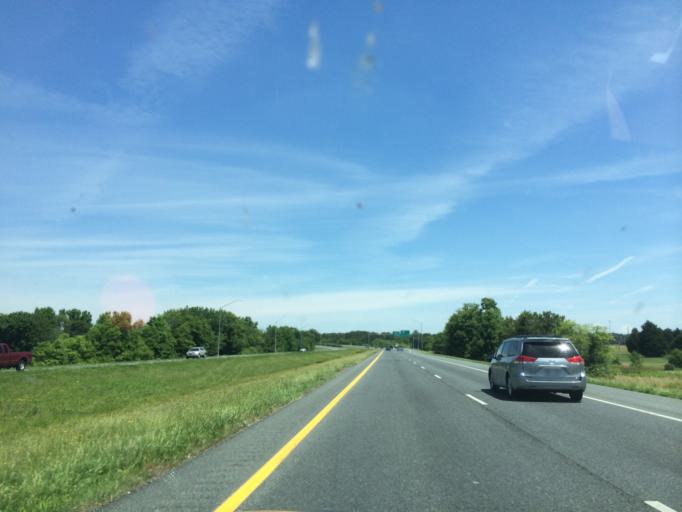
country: US
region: Maryland
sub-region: Wicomico County
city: Salisbury
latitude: 38.3610
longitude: -75.5385
